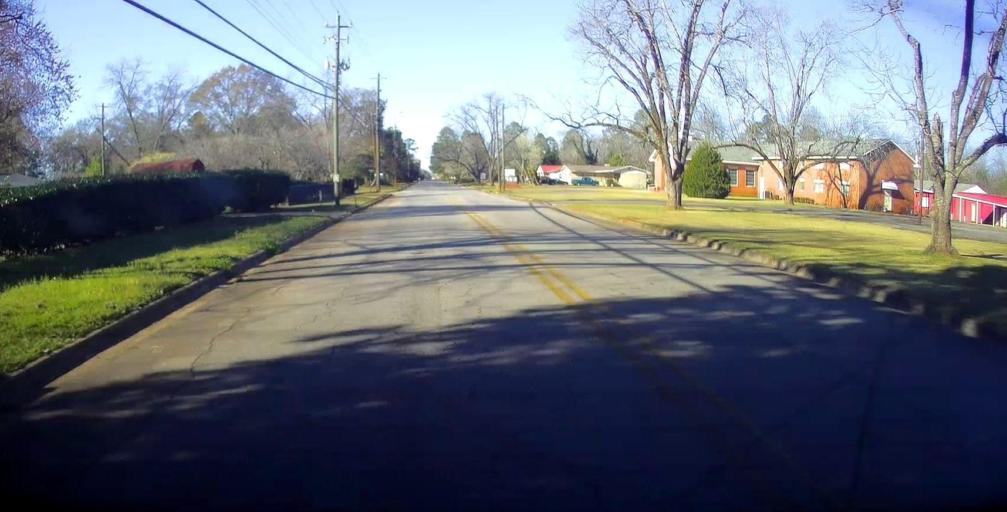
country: US
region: Georgia
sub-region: Peach County
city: Fort Valley
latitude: 32.5674
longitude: -83.8933
